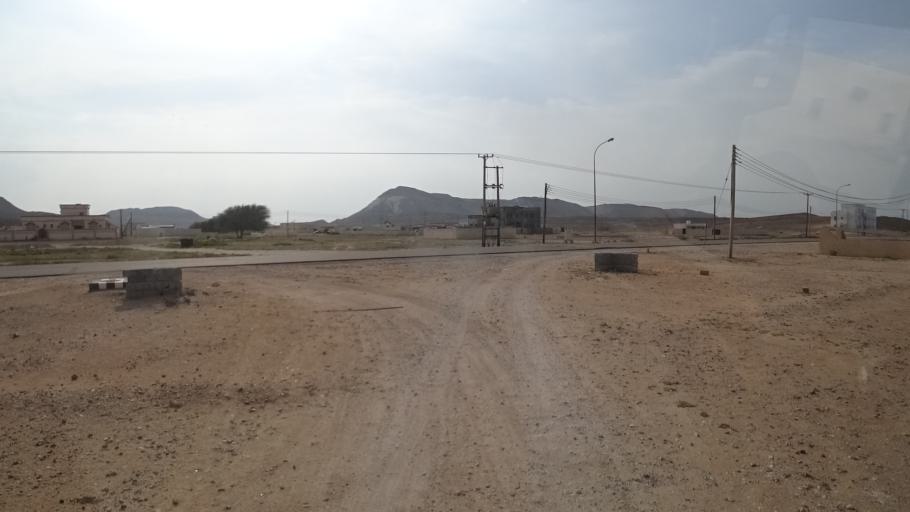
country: OM
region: Ash Sharqiyah
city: Sur
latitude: 22.4327
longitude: 59.8255
